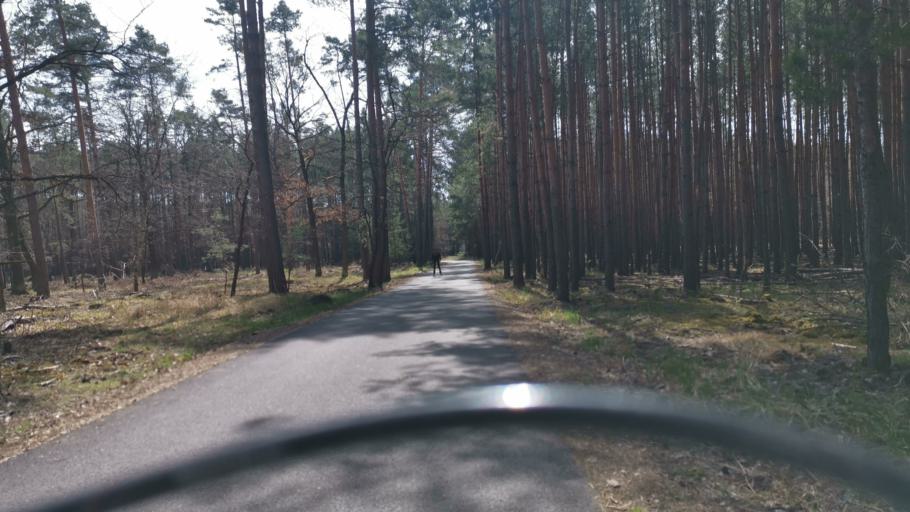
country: SK
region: Trnavsky
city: Gbely
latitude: 48.7173
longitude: 17.0525
